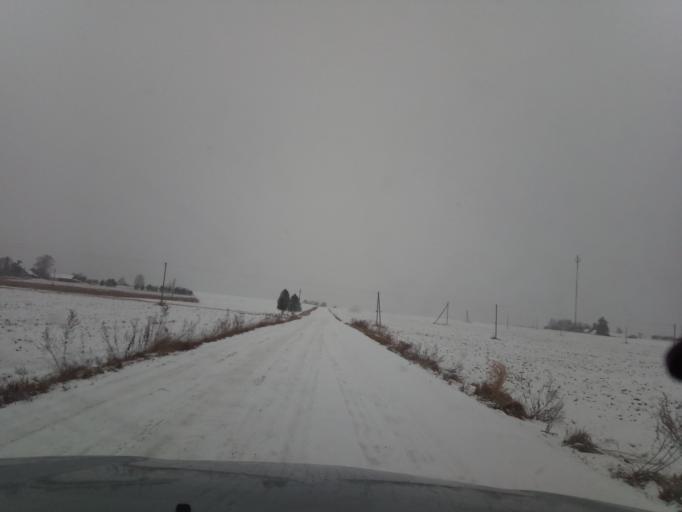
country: LT
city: Ramygala
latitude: 55.5648
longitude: 24.3410
